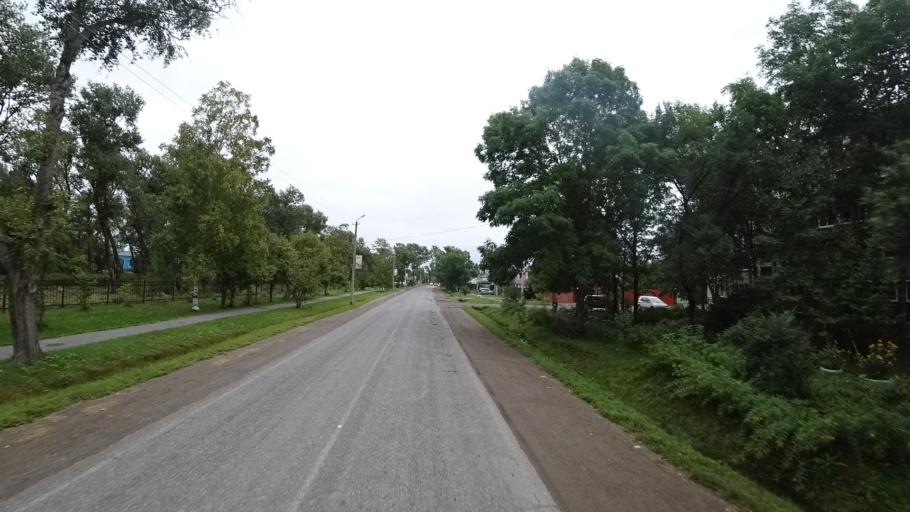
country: RU
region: Primorskiy
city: Chernigovka
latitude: 44.3407
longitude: 132.5795
